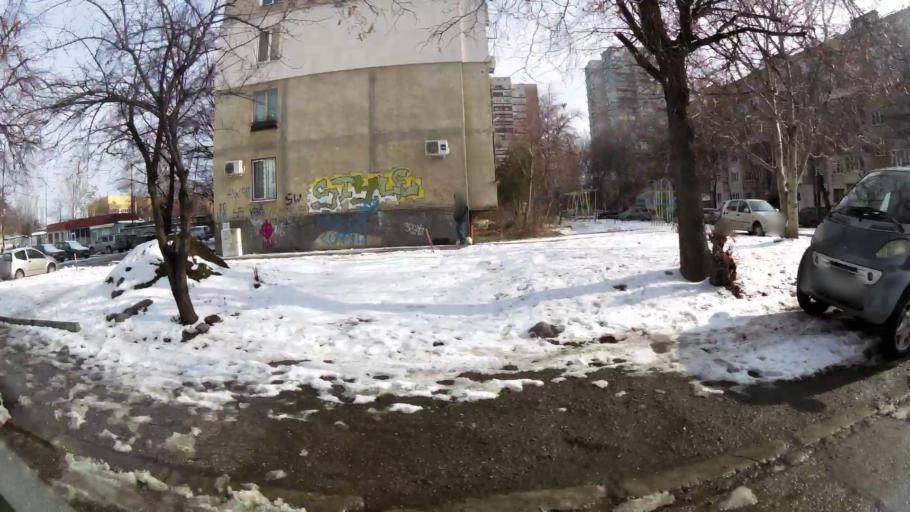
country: BG
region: Sofia-Capital
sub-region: Stolichna Obshtina
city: Sofia
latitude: 42.7102
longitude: 23.3612
